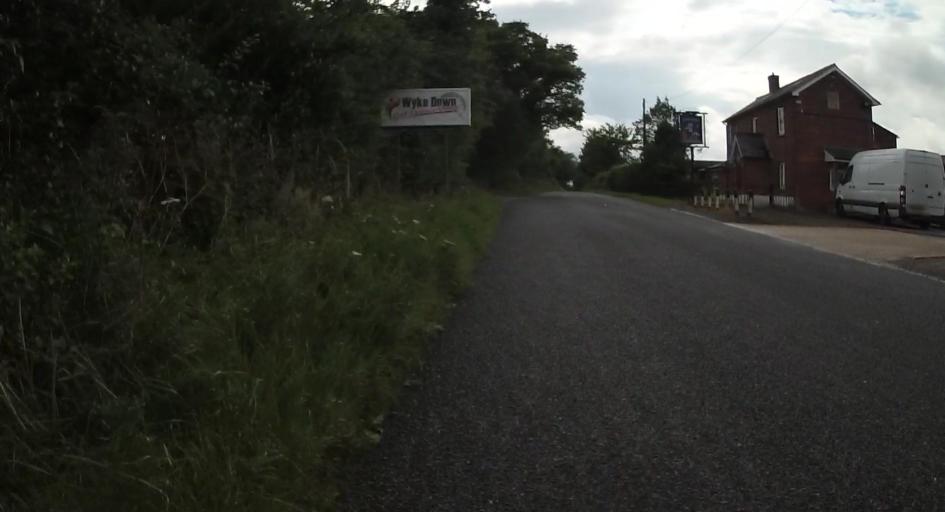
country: GB
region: England
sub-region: Hampshire
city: Andover
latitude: 51.2266
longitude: -1.4236
